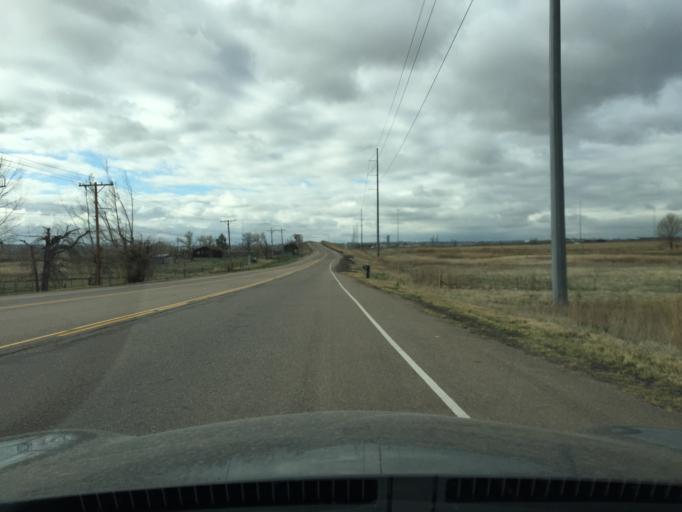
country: US
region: Colorado
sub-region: Boulder County
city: Erie
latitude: 39.9854
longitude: -104.9785
